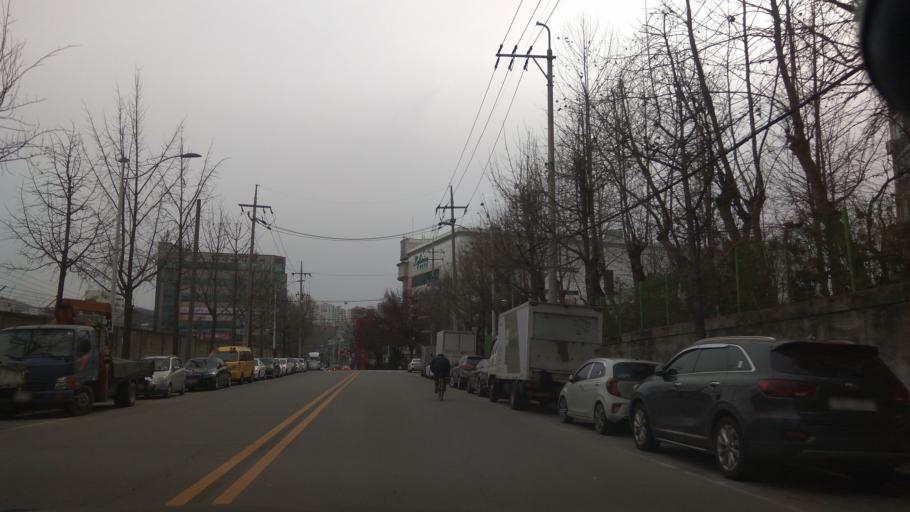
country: KR
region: Incheon
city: Incheon
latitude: 37.4921
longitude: 126.7104
